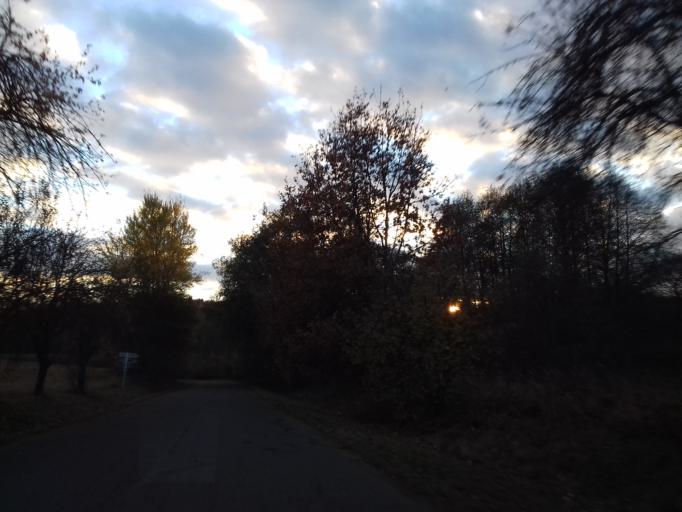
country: CZ
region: Pardubicky
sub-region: Okres Chrudim
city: Skutec
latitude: 49.8324
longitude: 15.9820
